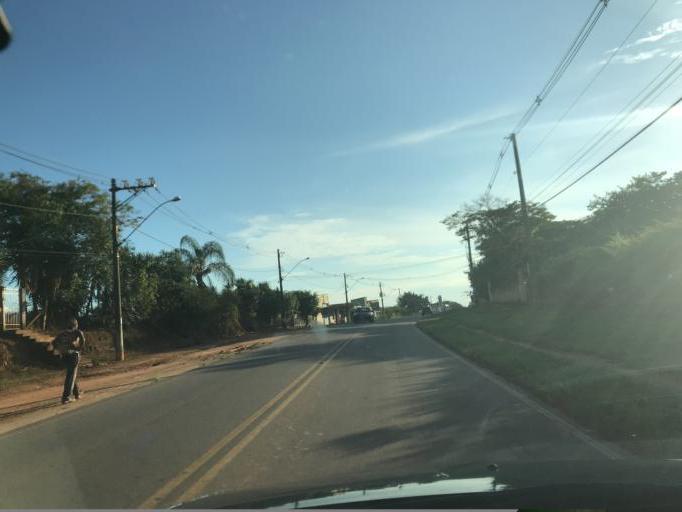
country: BR
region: Minas Gerais
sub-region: Tres Coracoes
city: Tres Coracoes
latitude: -21.6889
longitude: -45.2362
